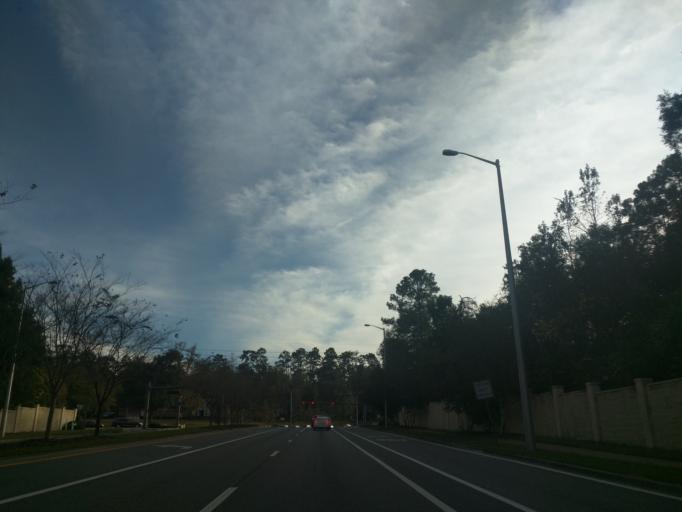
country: US
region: Florida
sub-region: Leon County
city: Tallahassee
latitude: 30.4537
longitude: -84.2487
